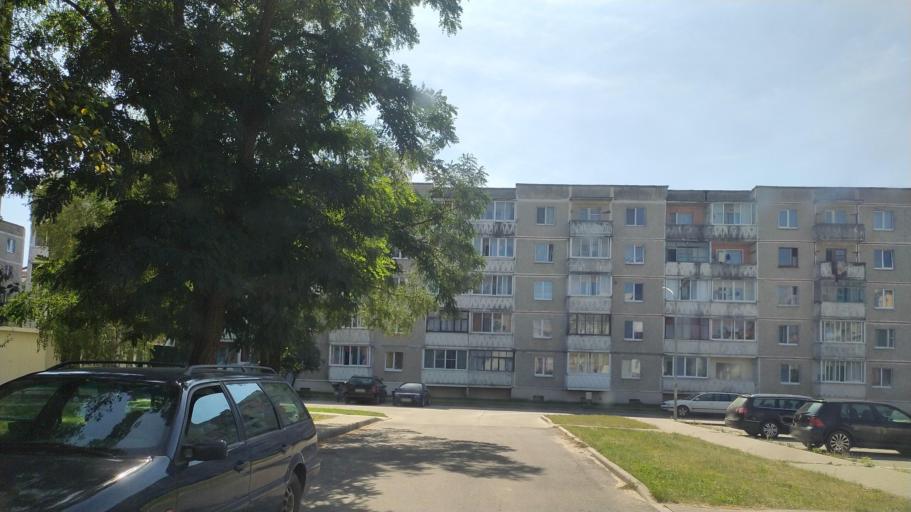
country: BY
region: Brest
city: Byaroza
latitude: 52.5373
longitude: 24.9946
